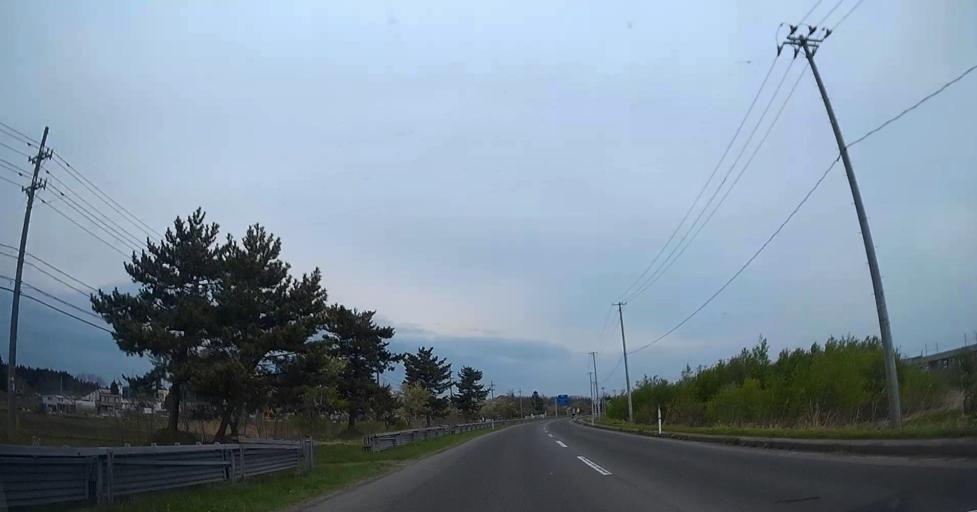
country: JP
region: Aomori
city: Aomori Shi
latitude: 40.8467
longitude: 140.6837
